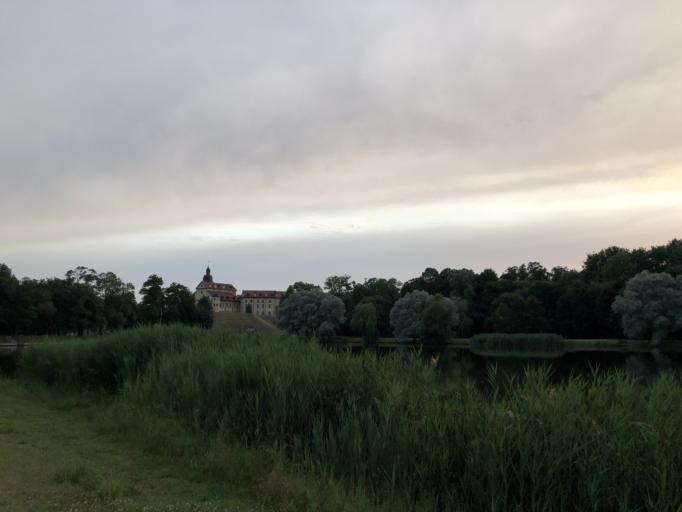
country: BY
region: Minsk
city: Nyasvizh
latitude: 53.2238
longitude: 26.6975
